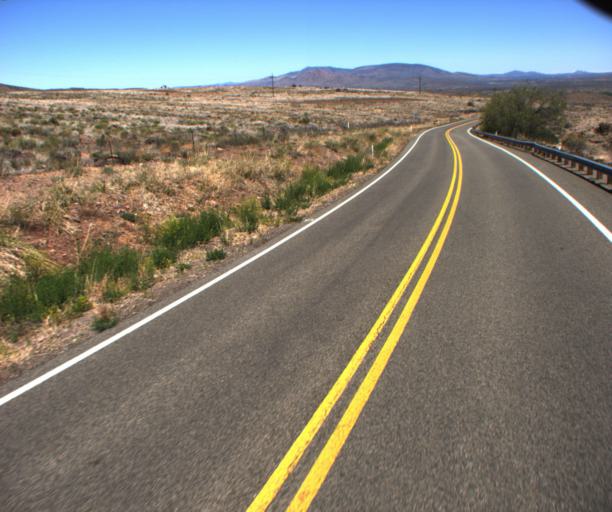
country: US
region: Arizona
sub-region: Yavapai County
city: Congress
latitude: 34.3322
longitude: -112.6868
